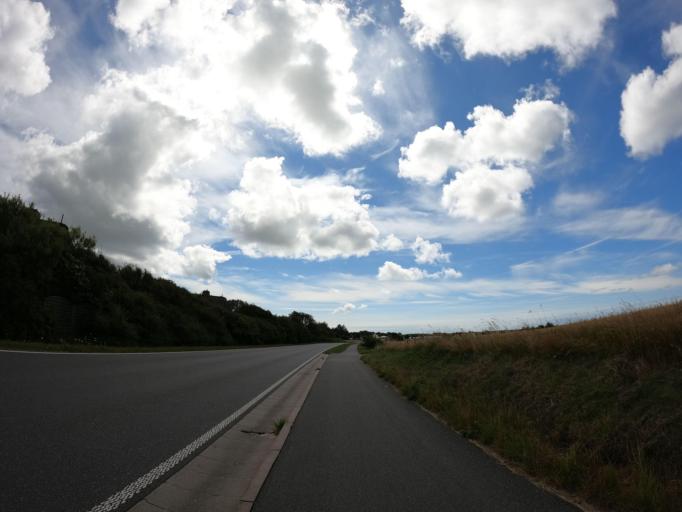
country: DE
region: Schleswig-Holstein
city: Keitum
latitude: 54.8982
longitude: 8.3651
